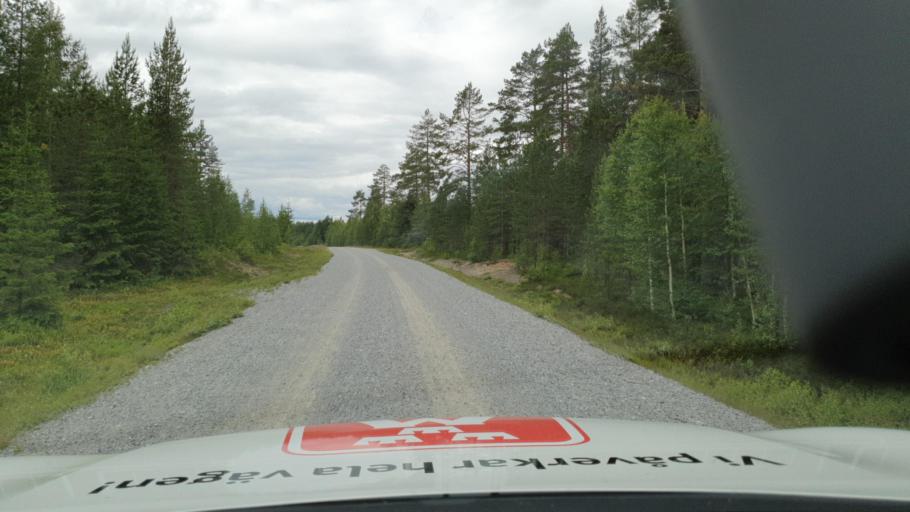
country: SE
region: Vaesterbotten
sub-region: Nordmalings Kommun
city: Nordmaling
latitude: 63.7381
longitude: 19.4092
